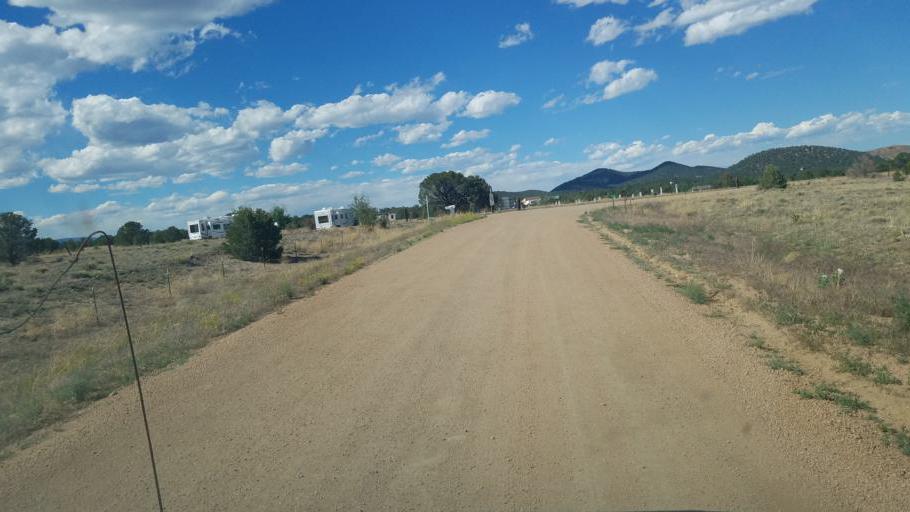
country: US
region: Colorado
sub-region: Custer County
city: Westcliffe
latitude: 38.2847
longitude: -105.5242
